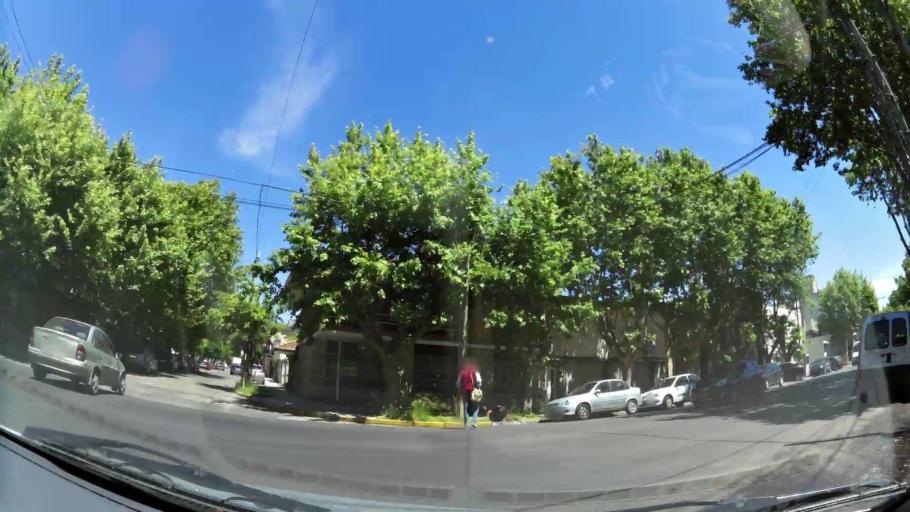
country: AR
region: Buenos Aires
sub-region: Partido de Quilmes
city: Quilmes
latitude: -34.7242
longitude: -58.2648
